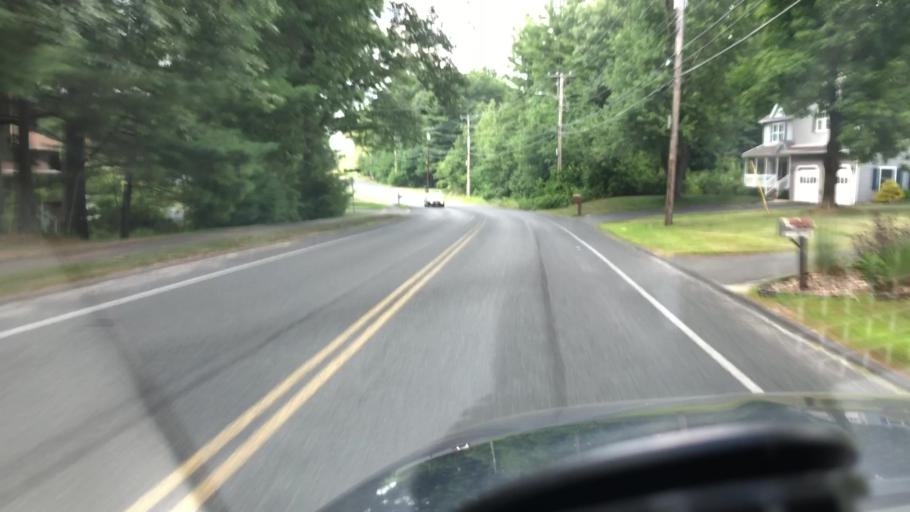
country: US
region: Massachusetts
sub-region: Hampshire County
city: Southampton
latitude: 42.1883
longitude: -72.6863
